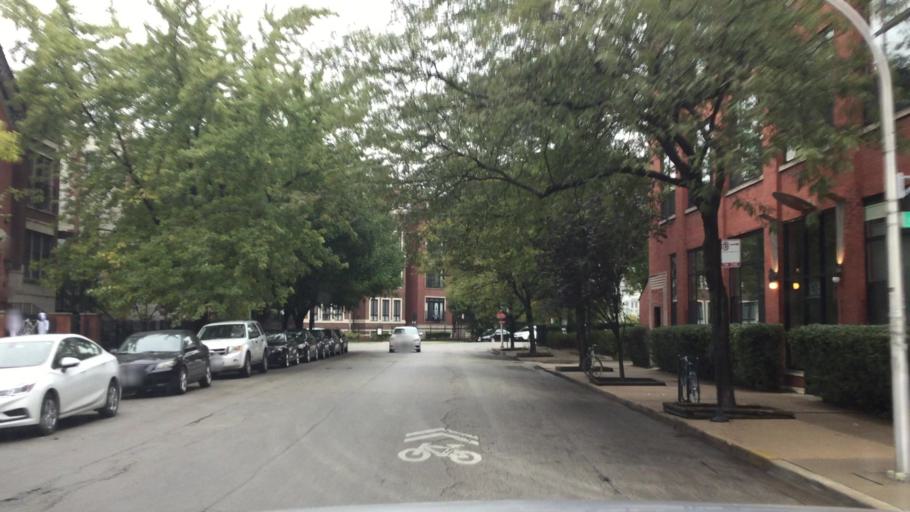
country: US
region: Illinois
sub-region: Cook County
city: Chicago
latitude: 41.9049
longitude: -87.6724
